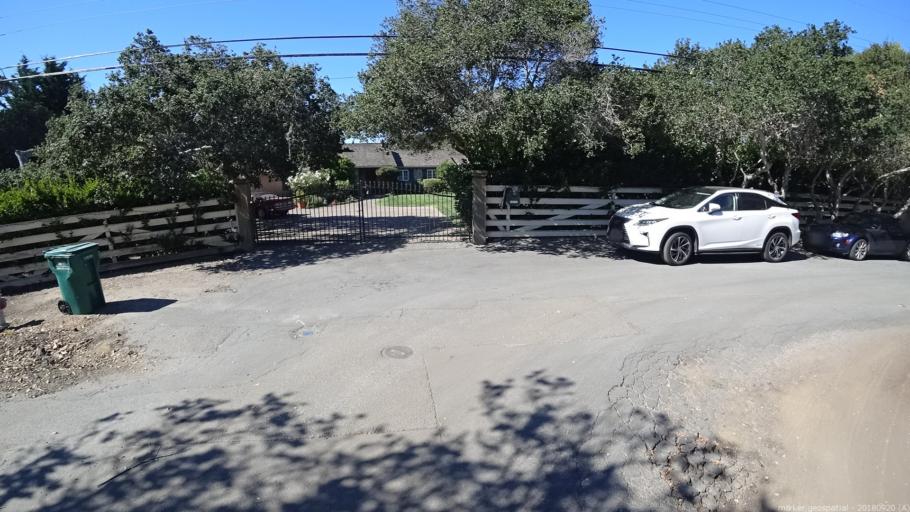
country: US
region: California
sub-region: Monterey County
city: Carmel-by-the-Sea
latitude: 36.5517
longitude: -121.8981
